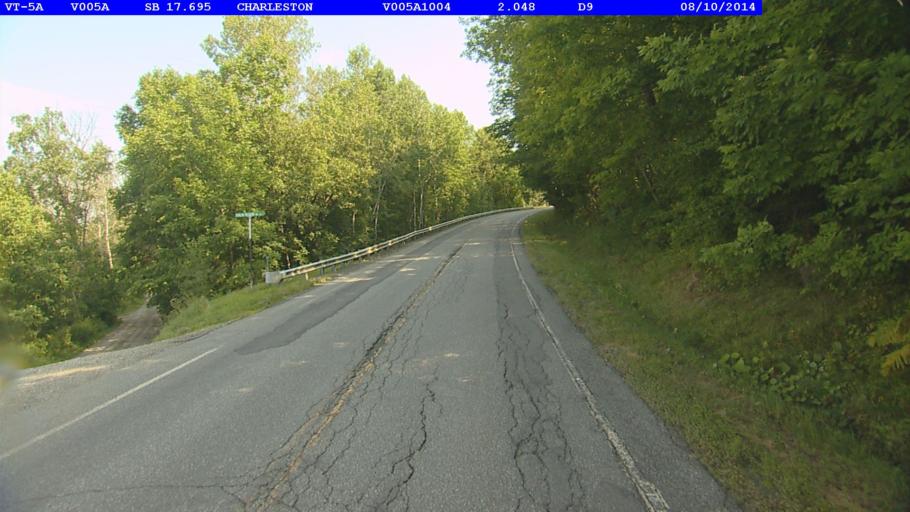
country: US
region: Vermont
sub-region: Orleans County
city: Newport
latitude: 44.8621
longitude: -72.0520
